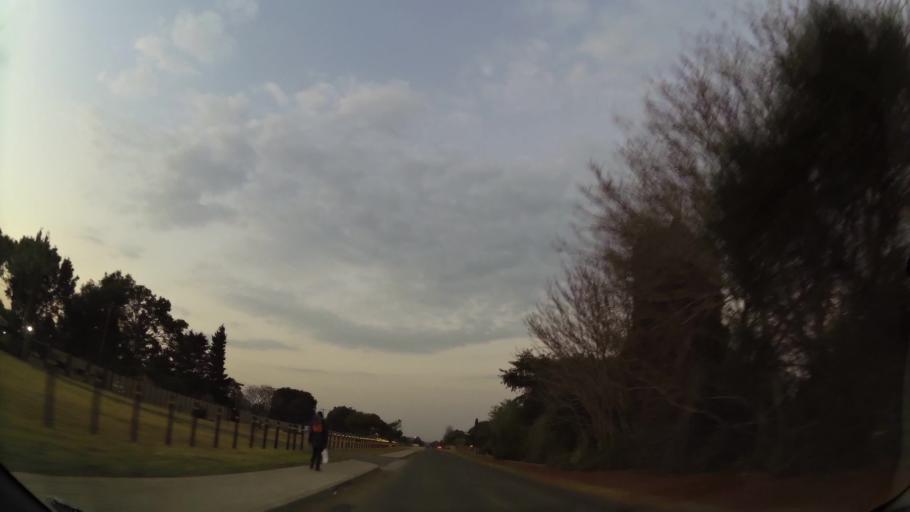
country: ZA
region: Gauteng
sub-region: Ekurhuleni Metropolitan Municipality
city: Benoni
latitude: -26.1414
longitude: 28.3104
